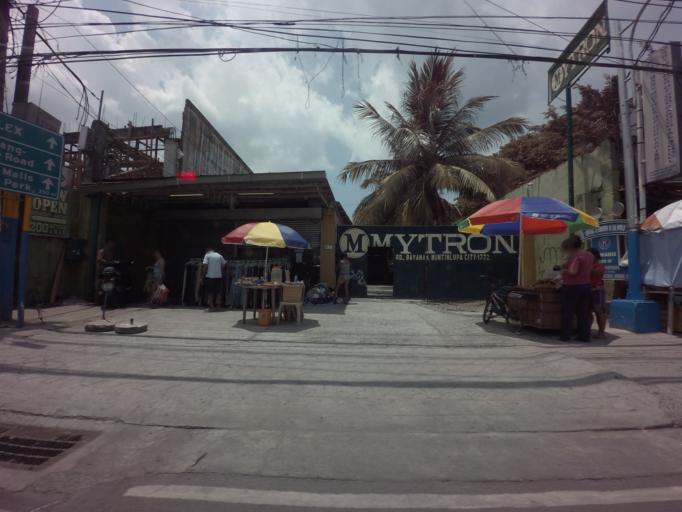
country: PH
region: Calabarzon
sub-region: Province of Laguna
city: San Pedro
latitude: 14.4082
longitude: 121.0466
